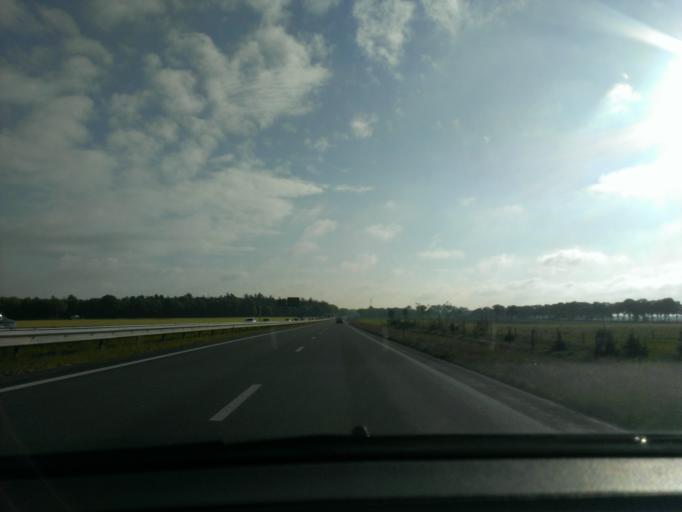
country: NL
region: Drenthe
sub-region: Gemeente Coevorden
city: Sleen
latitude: 52.7347
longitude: 6.7992
